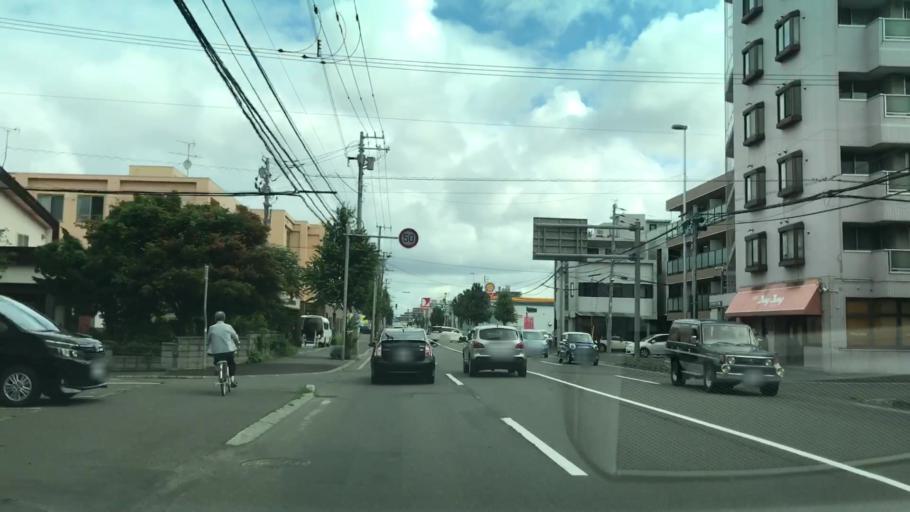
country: JP
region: Hokkaido
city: Sapporo
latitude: 43.0832
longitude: 141.3226
